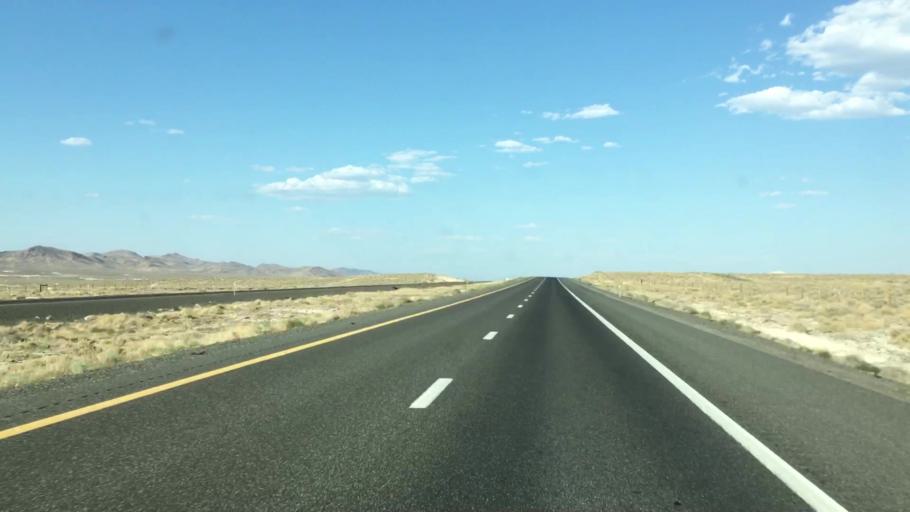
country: US
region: Nevada
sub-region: Lyon County
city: Fernley
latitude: 39.8344
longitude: -118.9605
